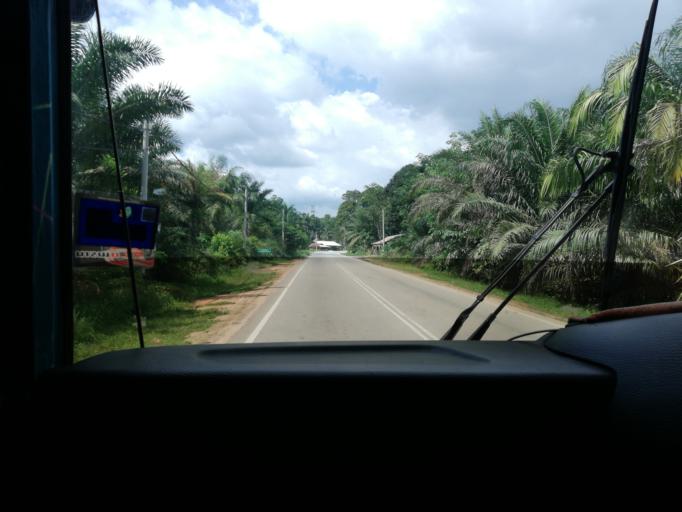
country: MY
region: Perak
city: Parit Buntar
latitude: 5.1238
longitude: 100.5674
